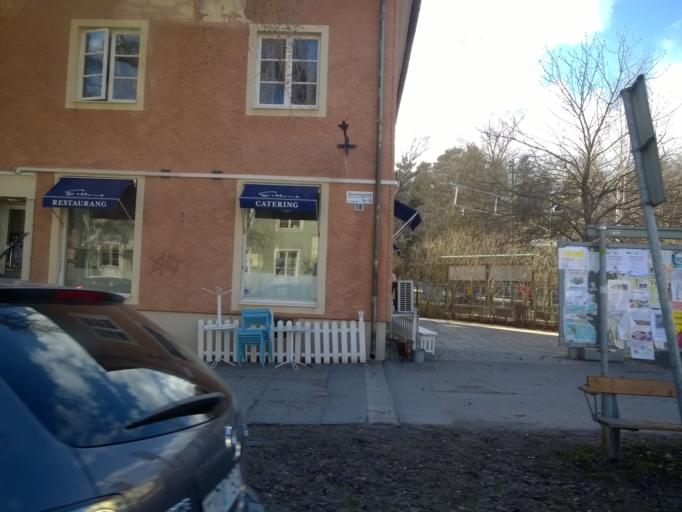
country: SE
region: Stockholm
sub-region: Stockholms Kommun
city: Bromma
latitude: 59.3232
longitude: 17.9564
